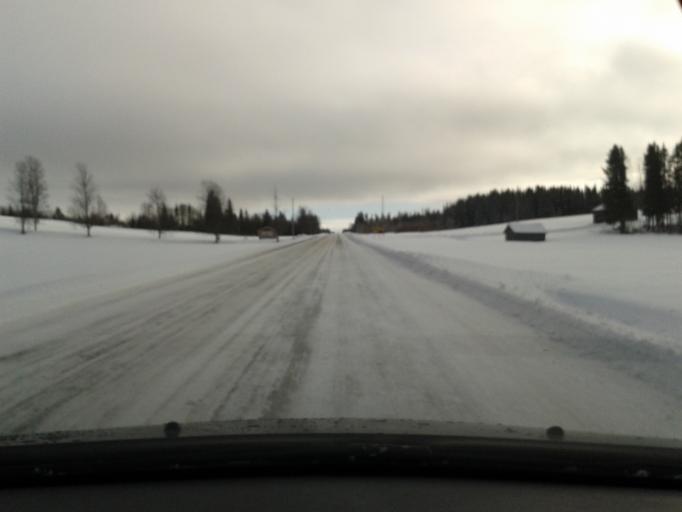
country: SE
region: Vaesterbotten
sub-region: Vilhelmina Kommun
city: Sjoberg
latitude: 64.7900
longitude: 16.0960
